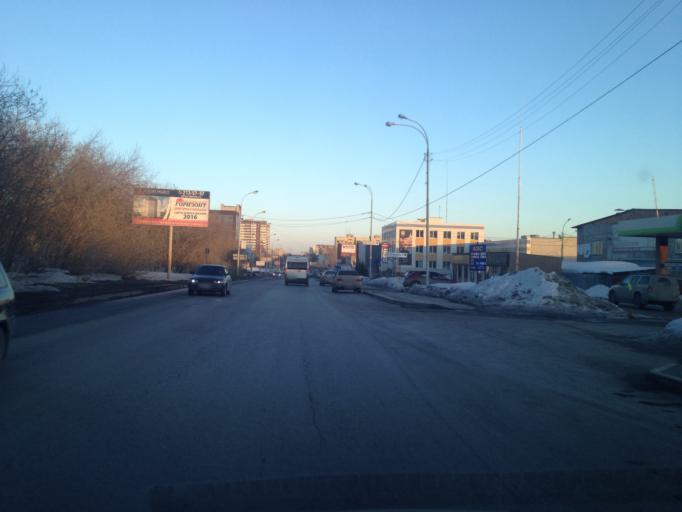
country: RU
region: Sverdlovsk
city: Sovkhoznyy
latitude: 56.8133
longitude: 60.5380
